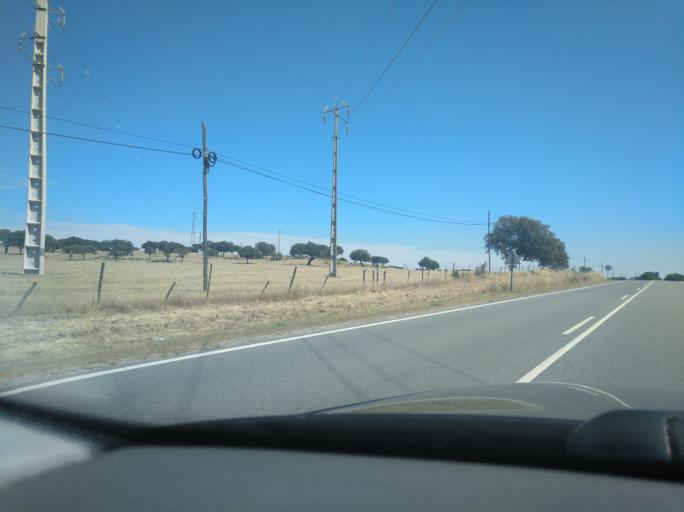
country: PT
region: Beja
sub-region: Almodovar
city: Almodovar
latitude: 37.5801
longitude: -8.0772
